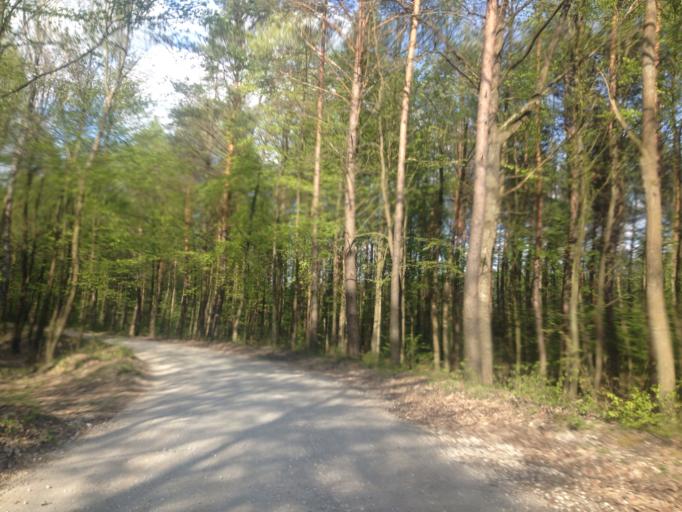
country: PL
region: Kujawsko-Pomorskie
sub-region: Powiat brodnicki
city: Gorzno
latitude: 53.2069
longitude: 19.7236
